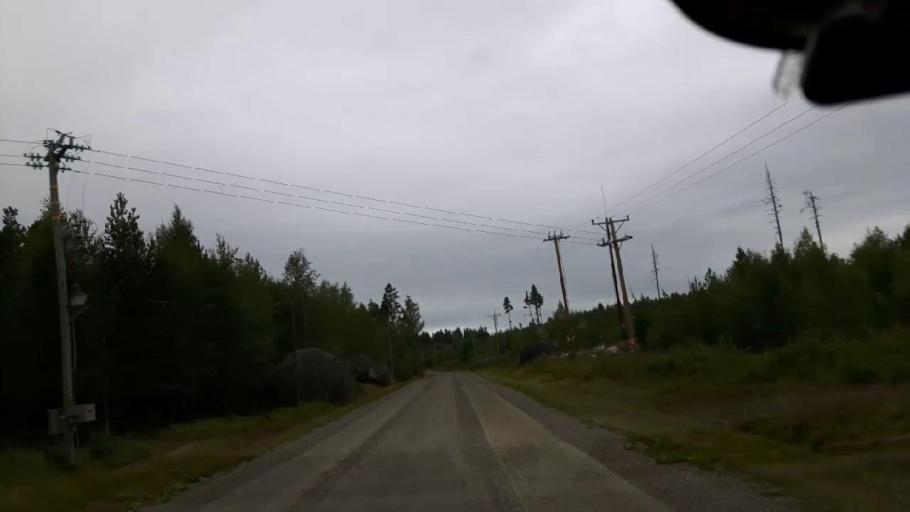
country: SE
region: Vaesternorrland
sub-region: Ange Kommun
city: Fransta
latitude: 62.7910
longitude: 16.0408
